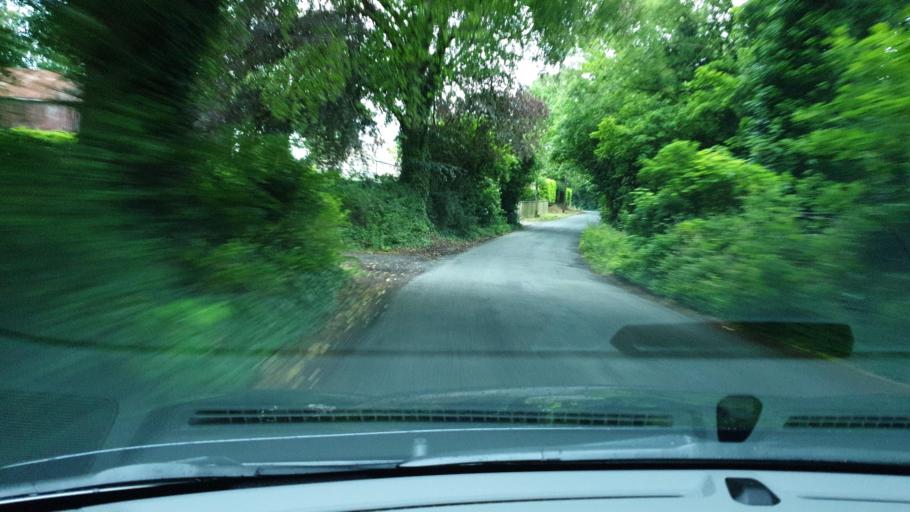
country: IE
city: Kentstown
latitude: 53.5998
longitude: -6.5952
